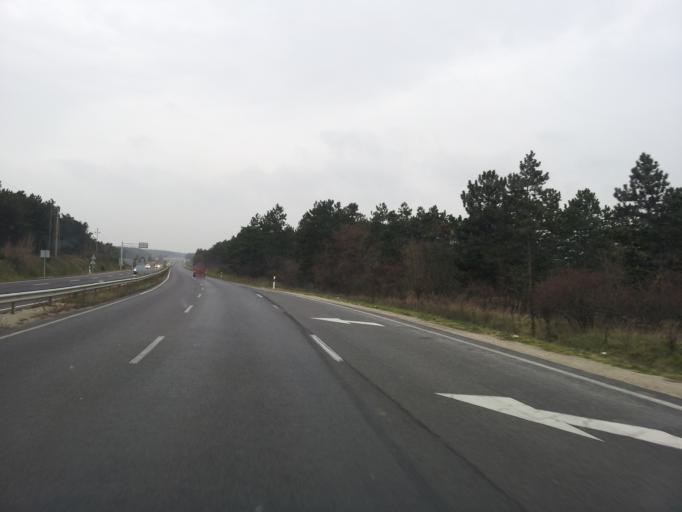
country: HU
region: Veszprem
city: Veszprem
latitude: 47.1090
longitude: 17.8645
